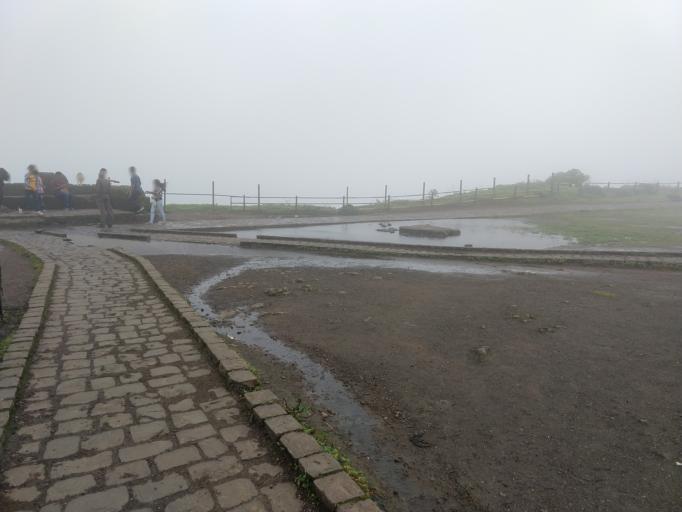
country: IN
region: Maharashtra
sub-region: Pune Division
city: Kharakvasla
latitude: 18.3667
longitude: 73.7516
